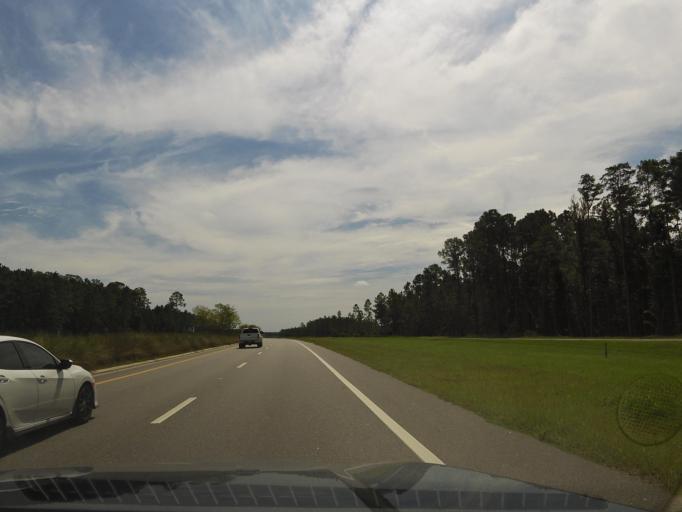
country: US
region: Florida
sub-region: Saint Johns County
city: Fruit Cove
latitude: 30.0235
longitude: -81.5201
